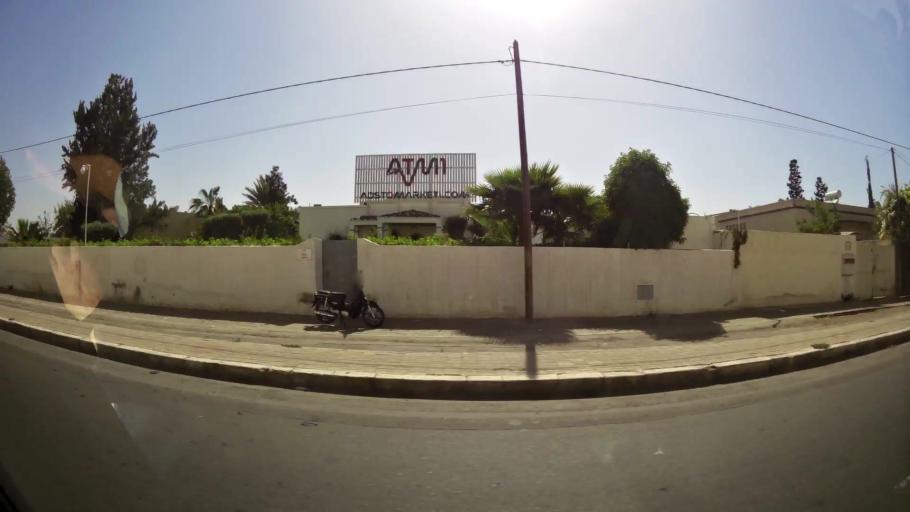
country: MA
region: Souss-Massa-Draa
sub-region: Inezgane-Ait Mellou
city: Inezgane
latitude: 30.3698
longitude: -9.5489
